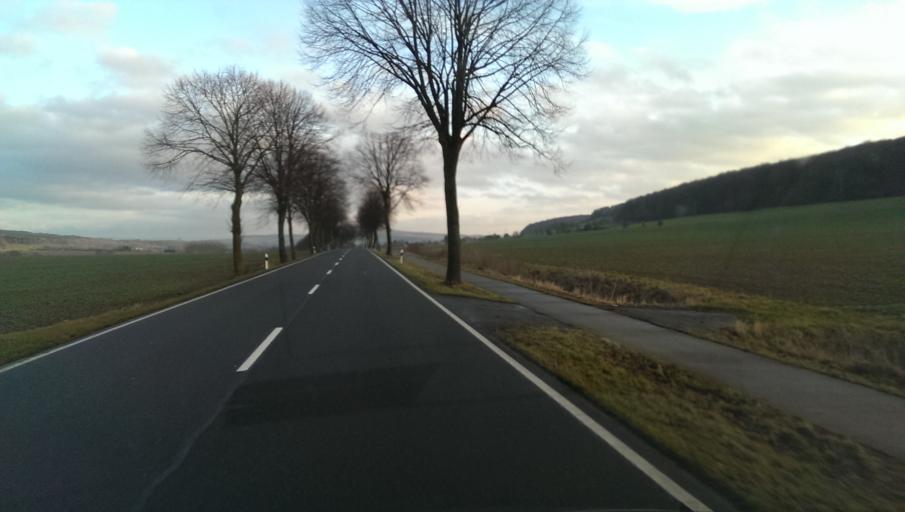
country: DE
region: Lower Saxony
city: Eimen
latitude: 51.8833
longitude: 9.7612
